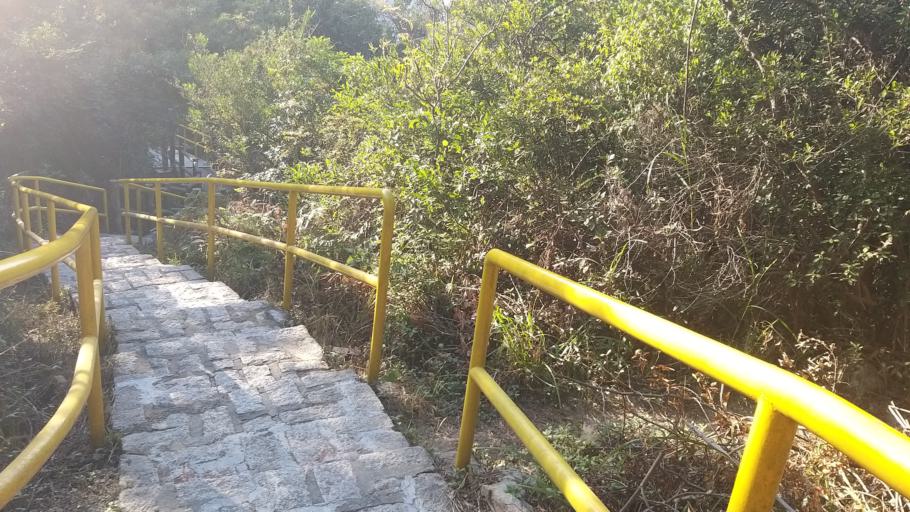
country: HK
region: Tuen Mun
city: Tuen Mun
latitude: 22.3951
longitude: 113.9827
